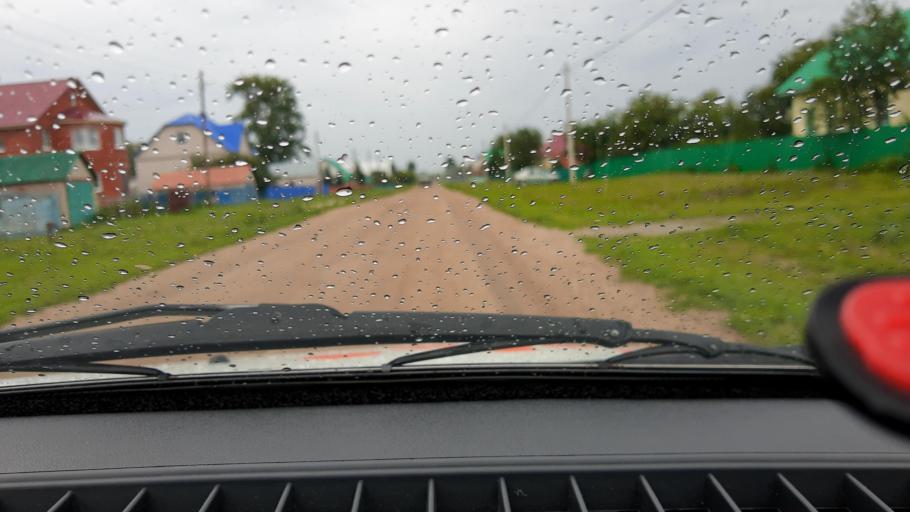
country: RU
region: Bashkortostan
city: Karmaskaly
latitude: 54.3805
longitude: 56.1129
